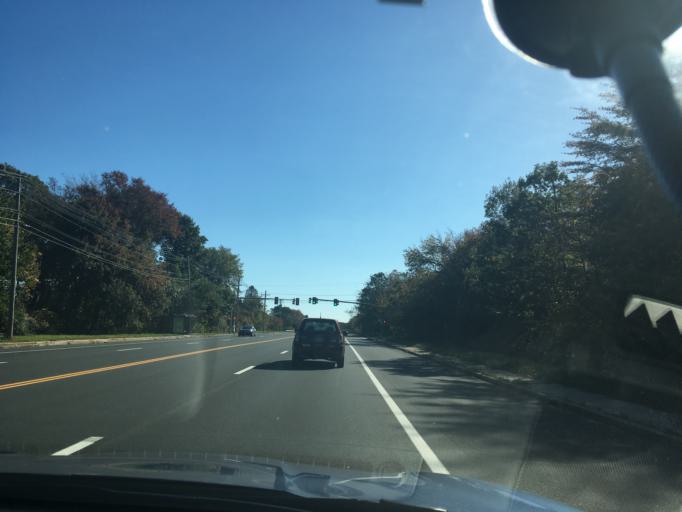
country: US
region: Rhode Island
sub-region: Washington County
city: Narragansett Pier
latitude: 41.4138
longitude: -71.4783
